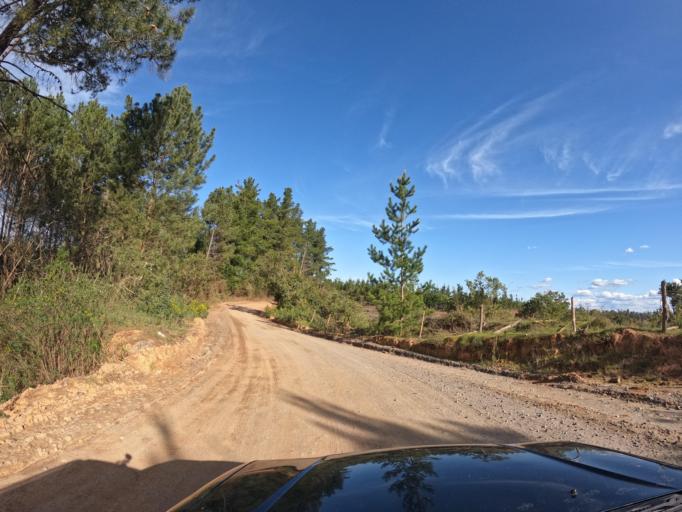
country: CL
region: Biobio
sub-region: Provincia de Biobio
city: La Laja
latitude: -37.1107
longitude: -72.7406
